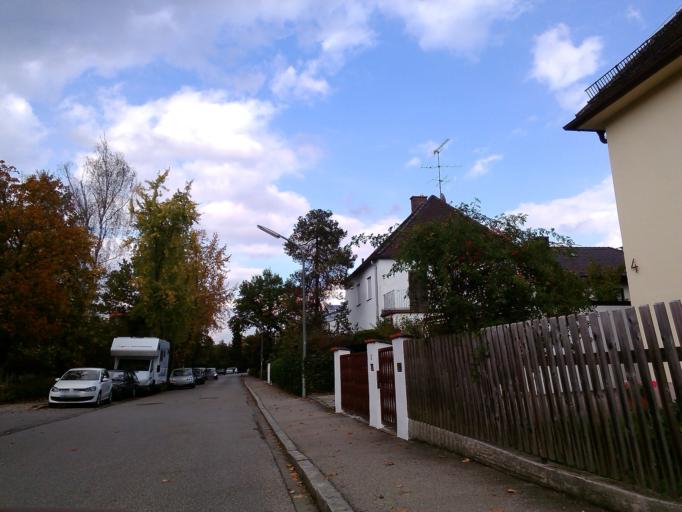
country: DE
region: Bavaria
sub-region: Upper Bavaria
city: Gauting
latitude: 48.0717
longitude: 11.3782
